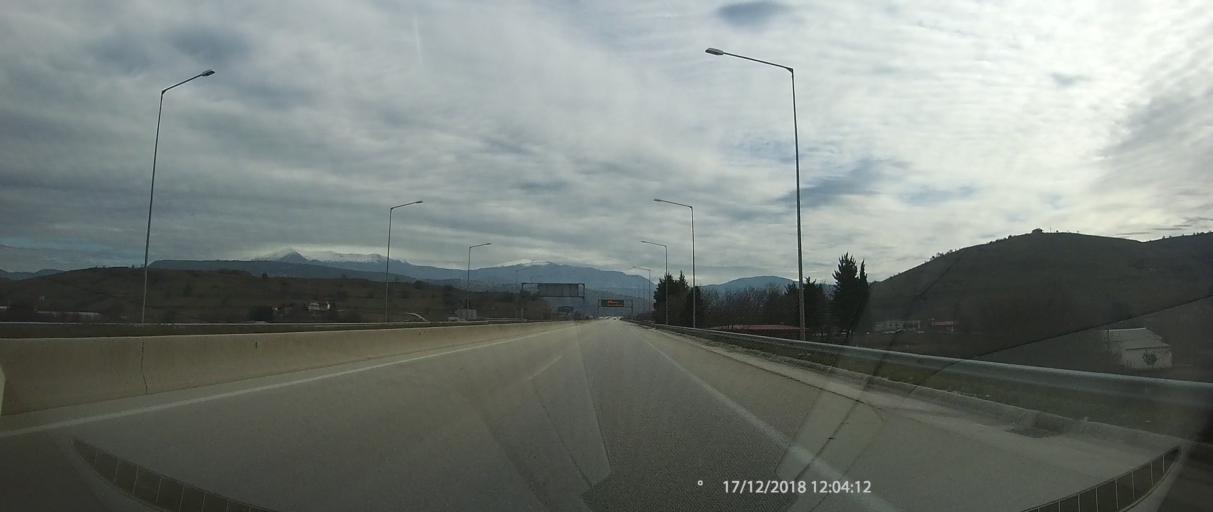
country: GR
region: Epirus
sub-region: Nomos Ioanninon
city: Katsikas
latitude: 39.6036
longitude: 20.8771
